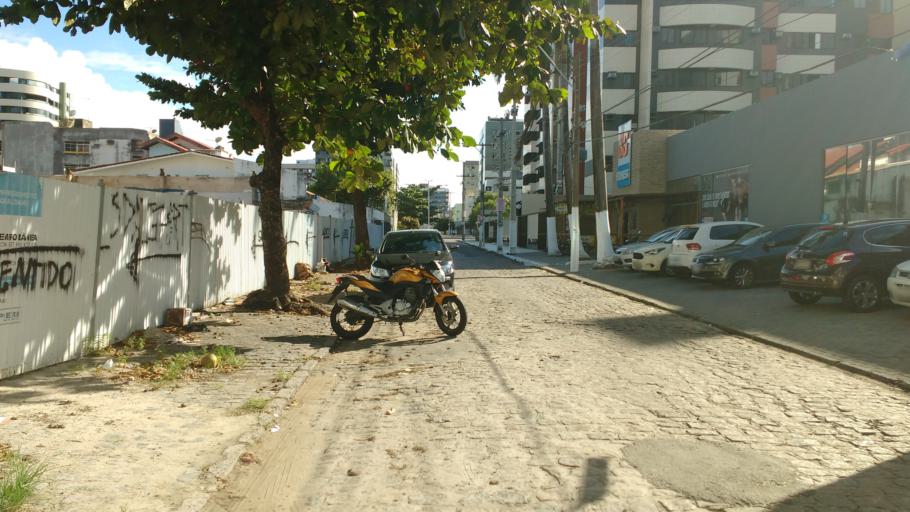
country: BR
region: Alagoas
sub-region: Maceio
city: Maceio
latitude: -9.6484
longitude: -35.7031
